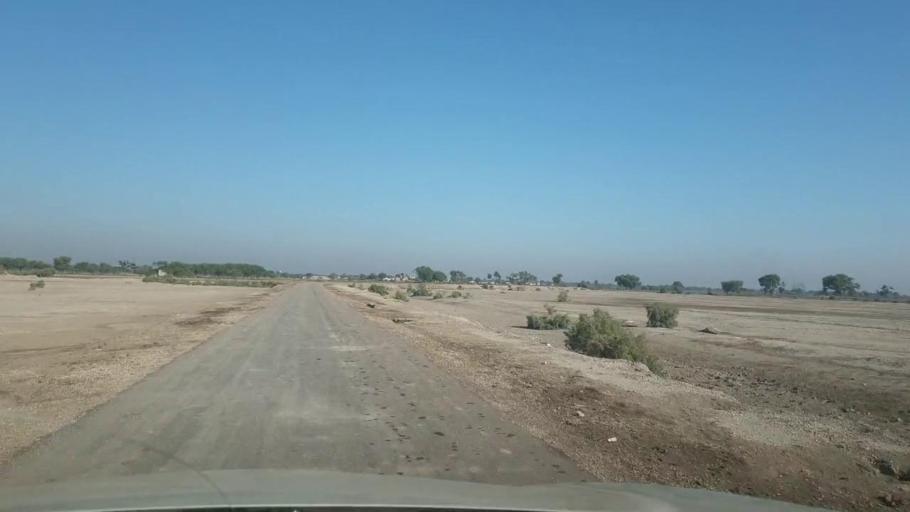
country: PK
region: Sindh
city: Bhan
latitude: 26.5256
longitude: 67.6739
